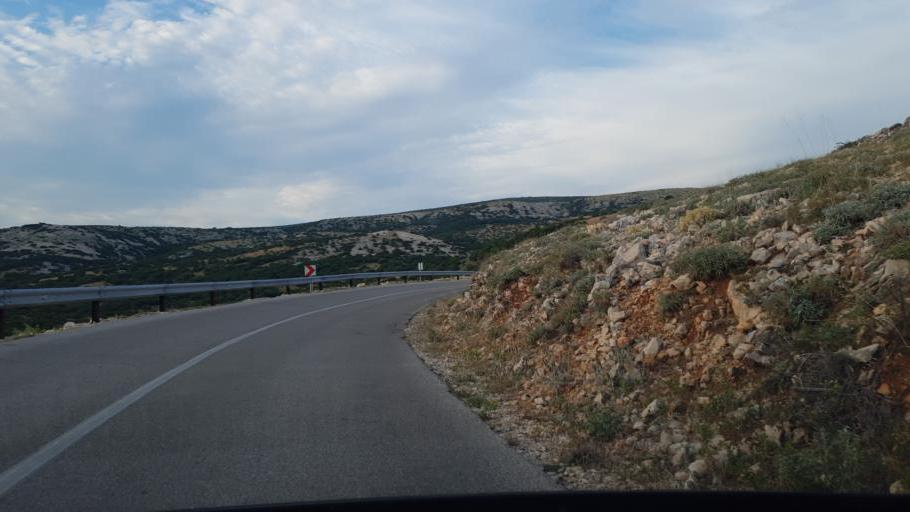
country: HR
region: Primorsko-Goranska
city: Punat
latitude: 44.9761
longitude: 14.6566
